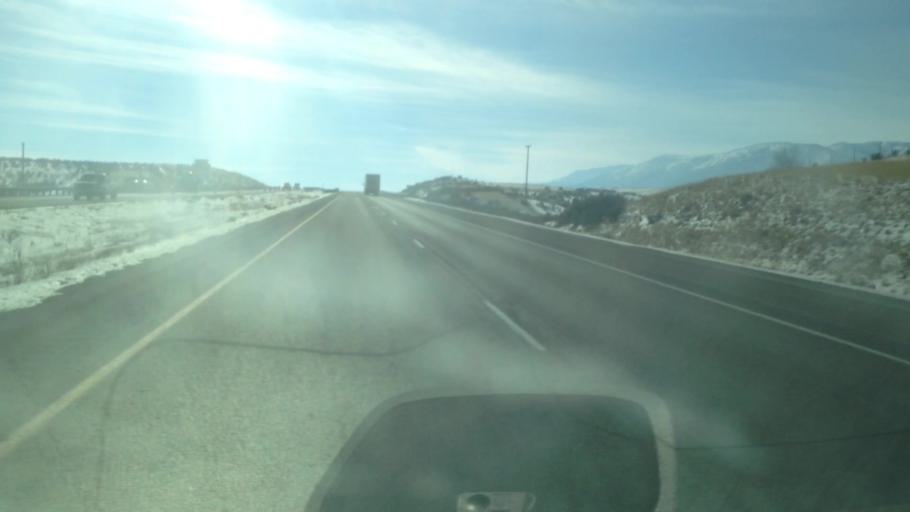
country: US
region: Idaho
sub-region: Oneida County
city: Malad City
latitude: 42.4134
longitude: -112.1905
